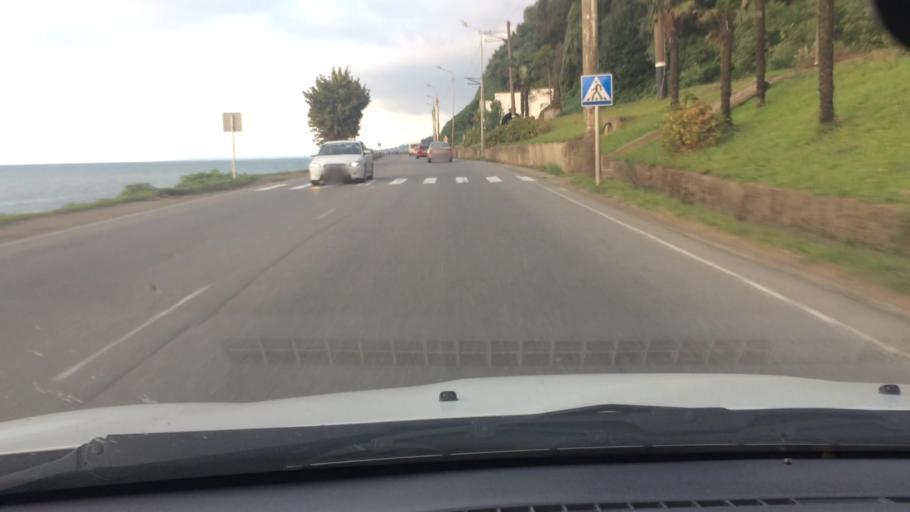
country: GE
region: Ajaria
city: Makhinjauri
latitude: 41.6691
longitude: 41.6874
